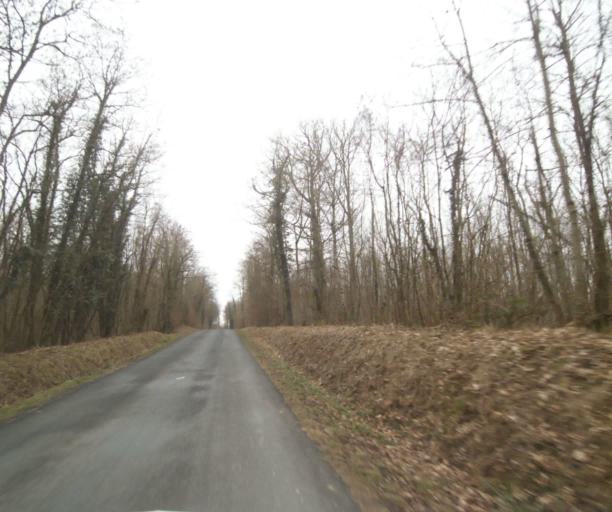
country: FR
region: Champagne-Ardenne
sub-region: Departement de la Haute-Marne
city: Bienville
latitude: 48.5685
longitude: 5.0187
